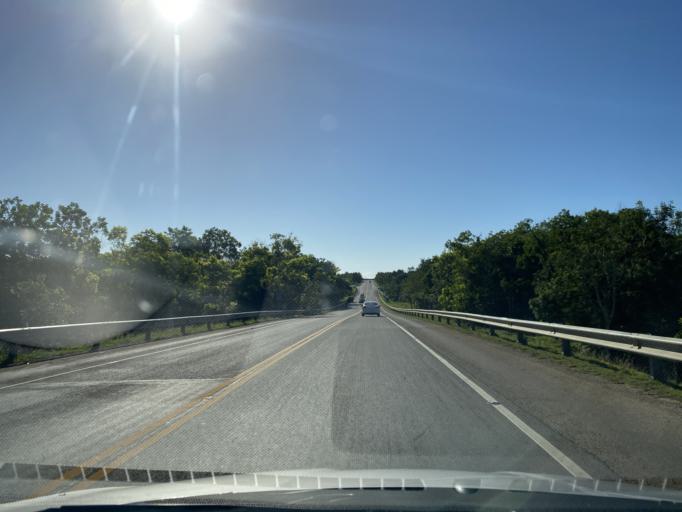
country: DO
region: Santo Domingo
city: Guerra
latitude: 18.5318
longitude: -69.7526
